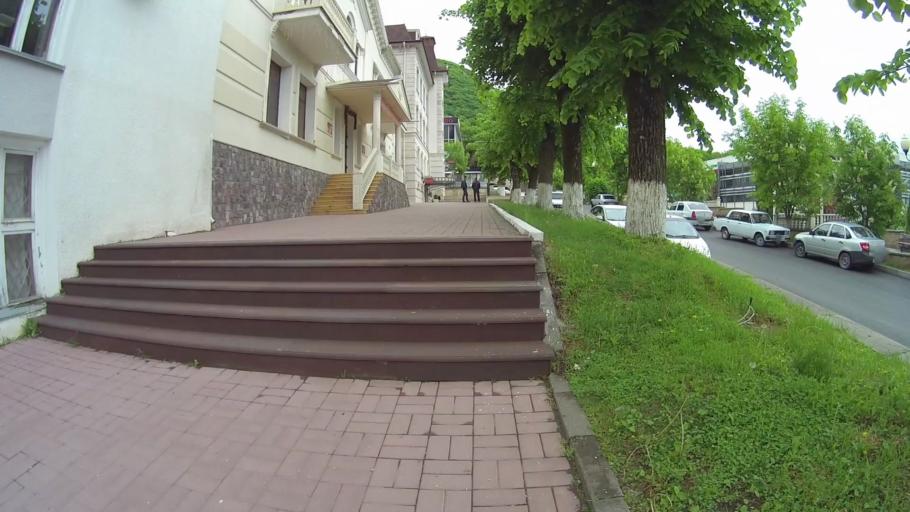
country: RU
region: Stavropol'skiy
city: Zheleznovodsk
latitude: 44.1327
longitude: 43.0304
